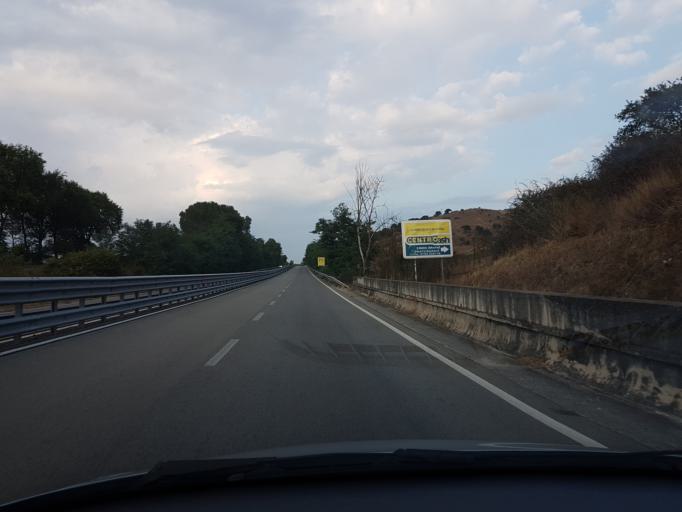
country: IT
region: Sardinia
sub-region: Provincia di Nuoro
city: Nuoro
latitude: 40.3178
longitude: 9.2585
